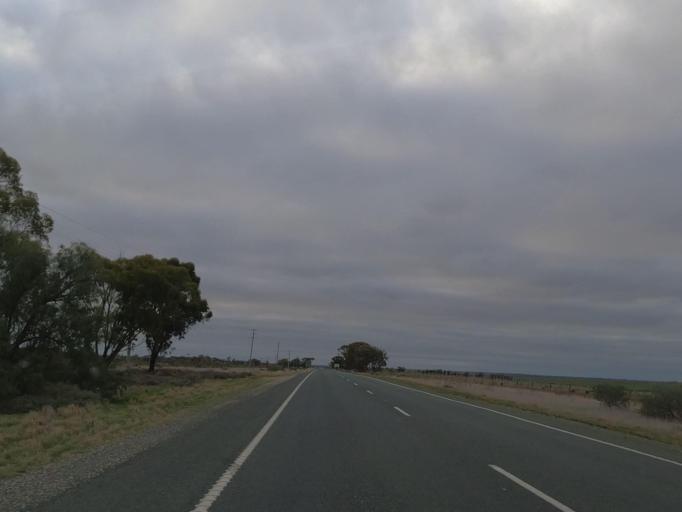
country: AU
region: Victoria
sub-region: Swan Hill
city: Swan Hill
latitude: -35.5705
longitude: 143.7858
